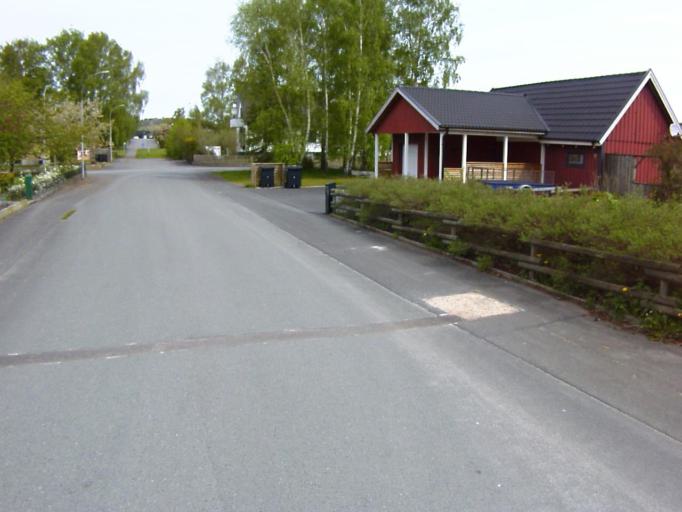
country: SE
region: Skane
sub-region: Kristianstads Kommun
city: Fjalkinge
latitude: 56.0404
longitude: 14.2723
